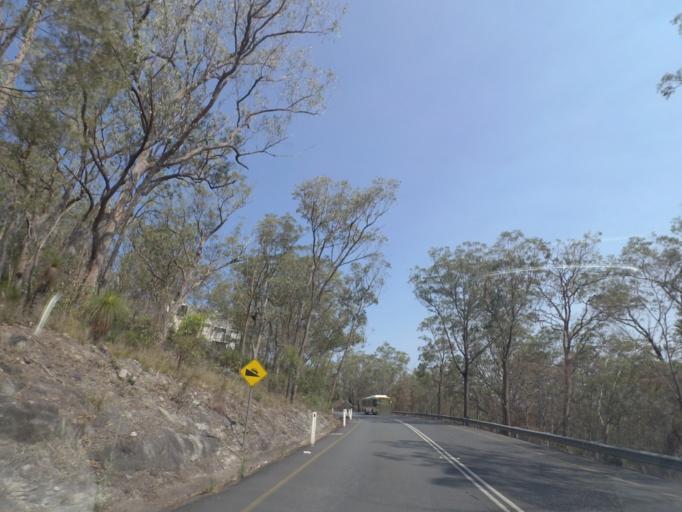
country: AU
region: Queensland
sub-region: Brisbane
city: Nathan
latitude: -27.5547
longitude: 153.0507
